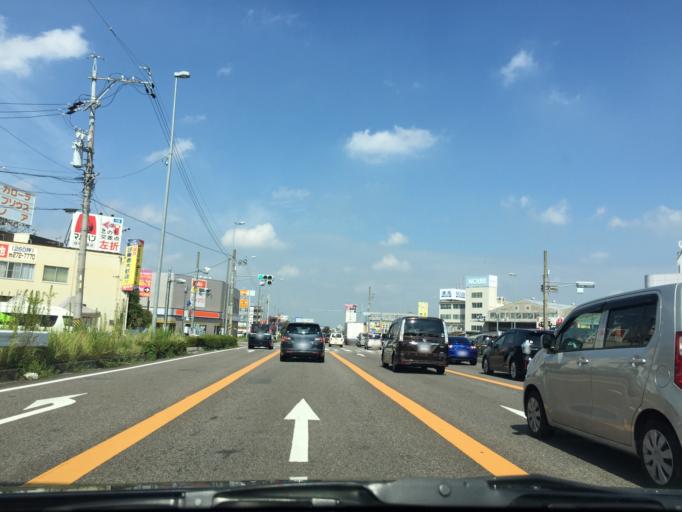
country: JP
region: Gifu
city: Kasamatsucho
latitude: 35.3914
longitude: 136.7379
